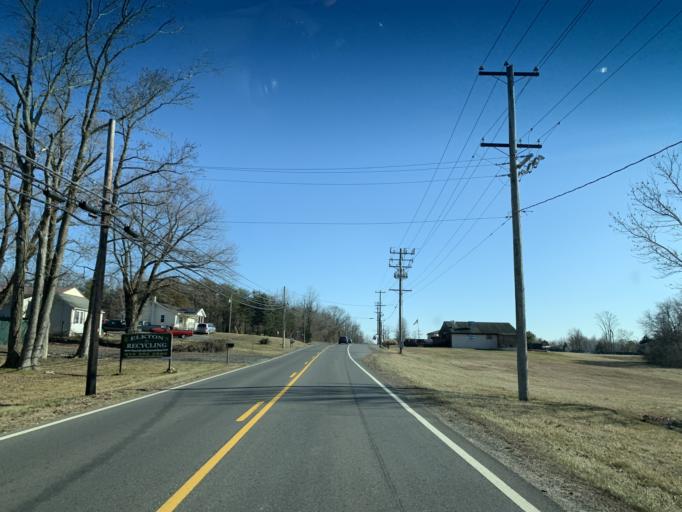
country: US
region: Maryland
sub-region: Cecil County
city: Elkton
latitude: 39.6227
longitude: -75.8526
